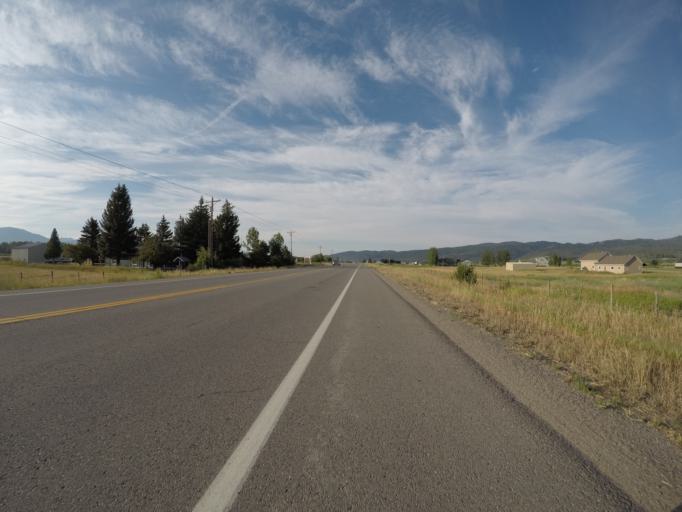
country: US
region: Wyoming
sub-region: Lincoln County
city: Afton
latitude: 42.9416
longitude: -111.0074
